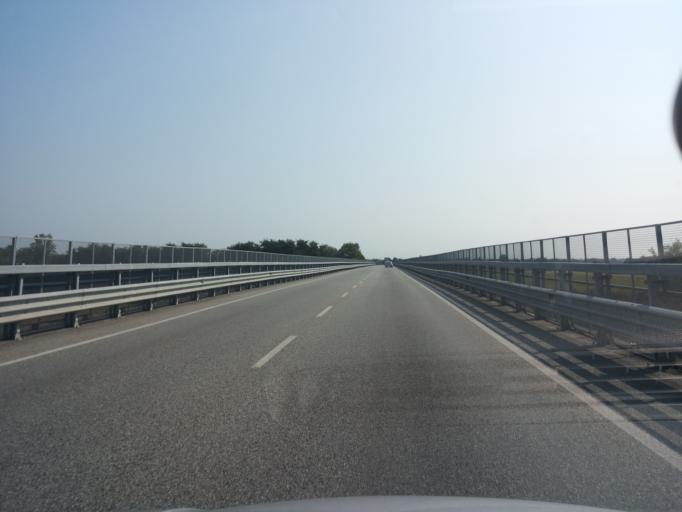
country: IT
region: Piedmont
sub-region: Provincia di Vercelli
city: Borgo Vercelli
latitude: 45.3447
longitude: 8.4403
